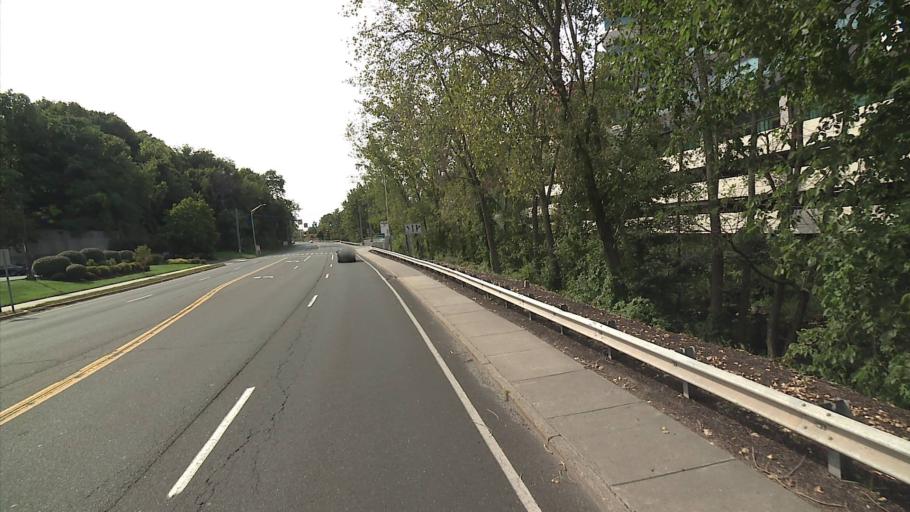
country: US
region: Connecticut
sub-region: Fairfield County
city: Norwalk
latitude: 41.1469
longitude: -73.4265
